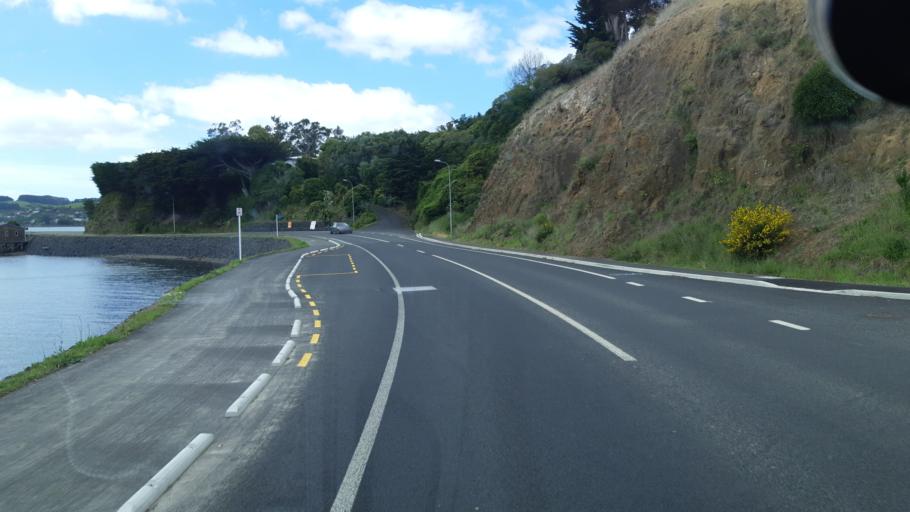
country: NZ
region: Otago
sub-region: Dunedin City
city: Portobello
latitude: -45.8763
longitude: 170.5798
